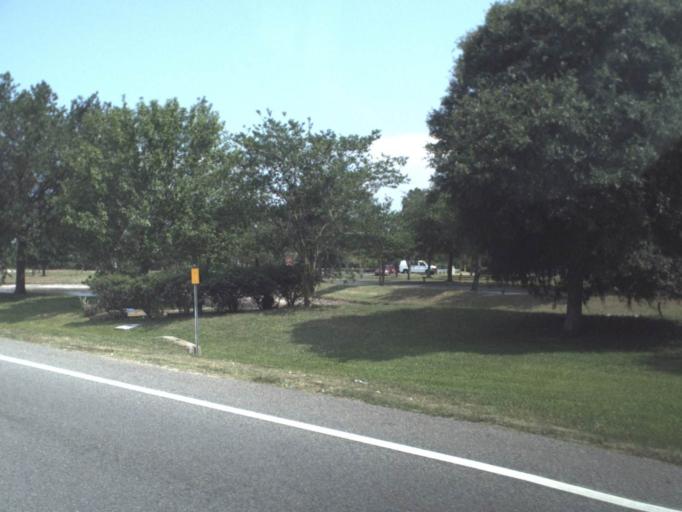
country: US
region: Florida
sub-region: Saint Johns County
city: Saint Augustine South
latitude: 29.8674
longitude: -81.3391
